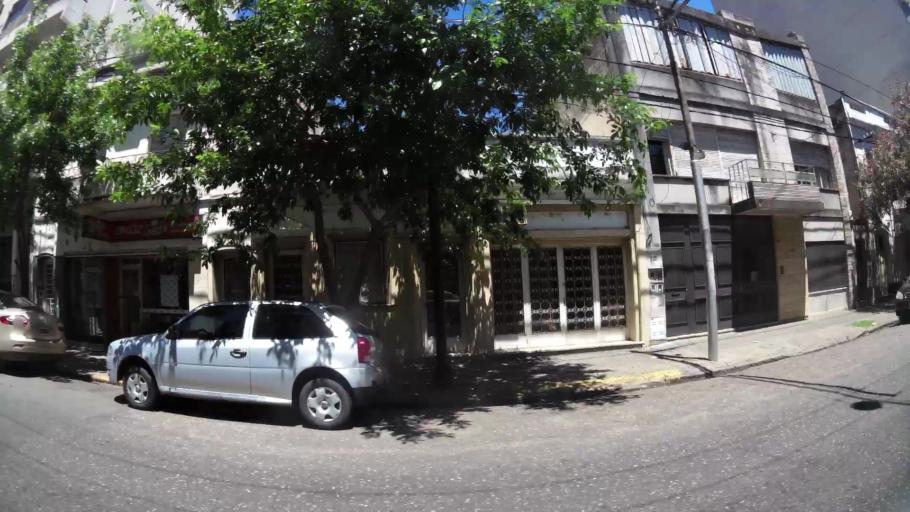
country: AR
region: Santa Fe
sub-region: Departamento de Rosario
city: Rosario
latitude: -32.9469
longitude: -60.6659
